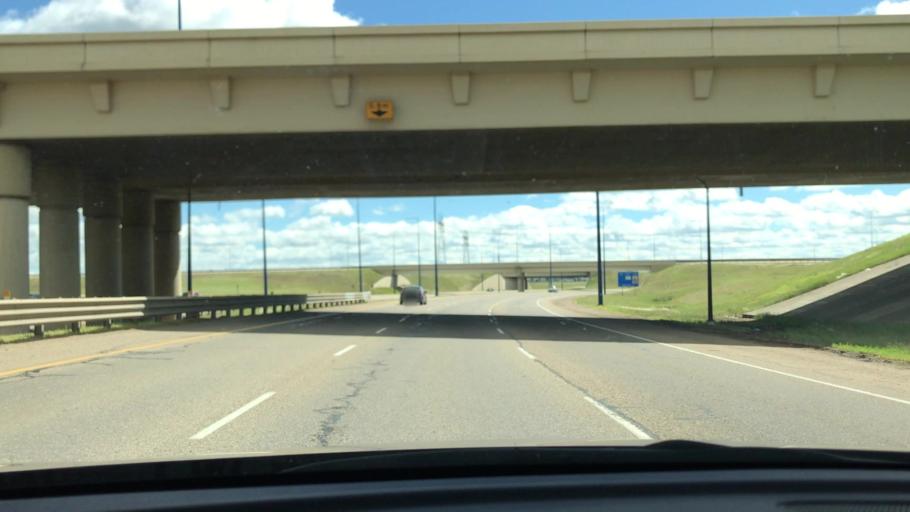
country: CA
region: Alberta
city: Beaumont
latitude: 53.4375
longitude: -113.4905
